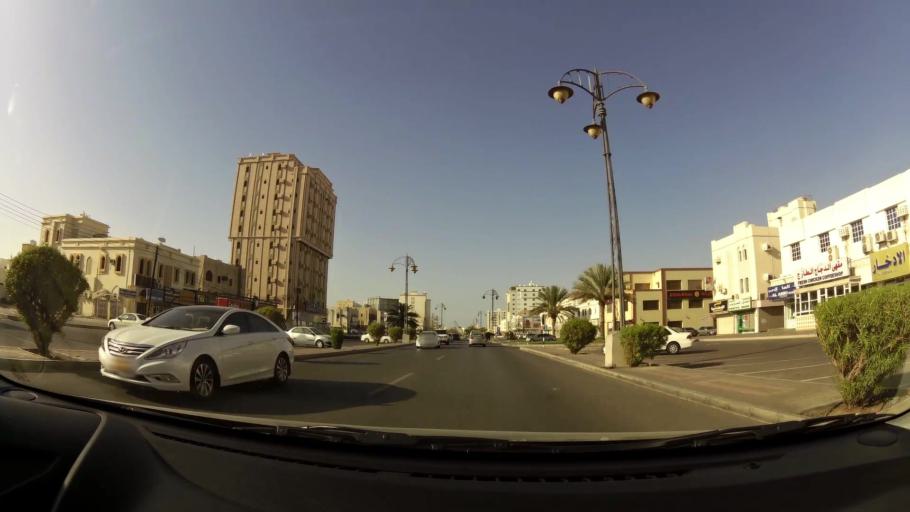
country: OM
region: Muhafazat Masqat
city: As Sib al Jadidah
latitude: 23.6279
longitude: 58.1960
